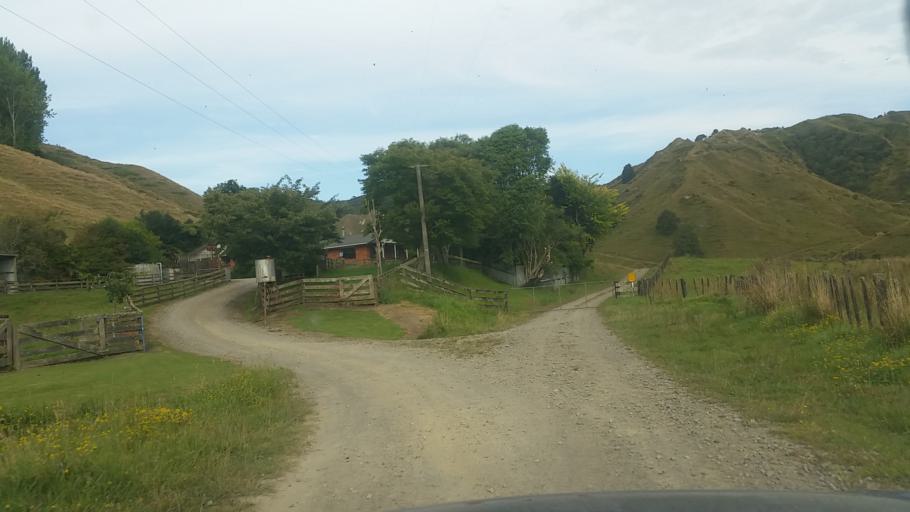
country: NZ
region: Taranaki
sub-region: New Plymouth District
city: Waitara
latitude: -39.1284
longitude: 174.6937
